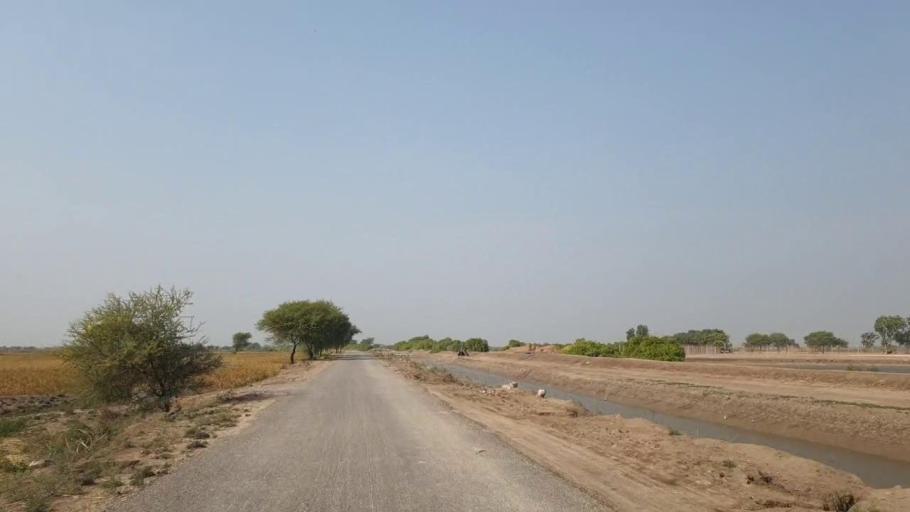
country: PK
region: Sindh
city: Matli
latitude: 24.9539
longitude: 68.5271
